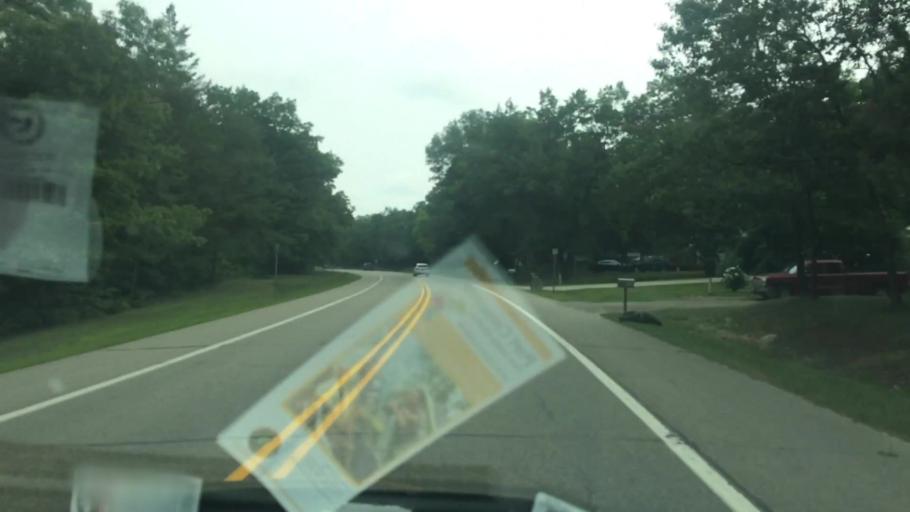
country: US
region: Michigan
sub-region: Huron County
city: Bad Axe
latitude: 43.9929
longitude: -83.0720
